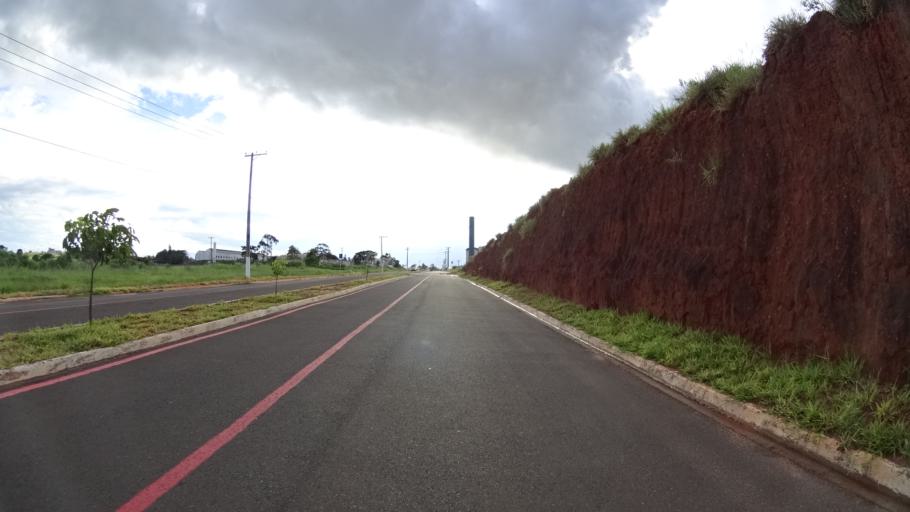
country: BR
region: Sao Paulo
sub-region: Marilia
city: Marilia
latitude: -22.2249
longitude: -49.8998
